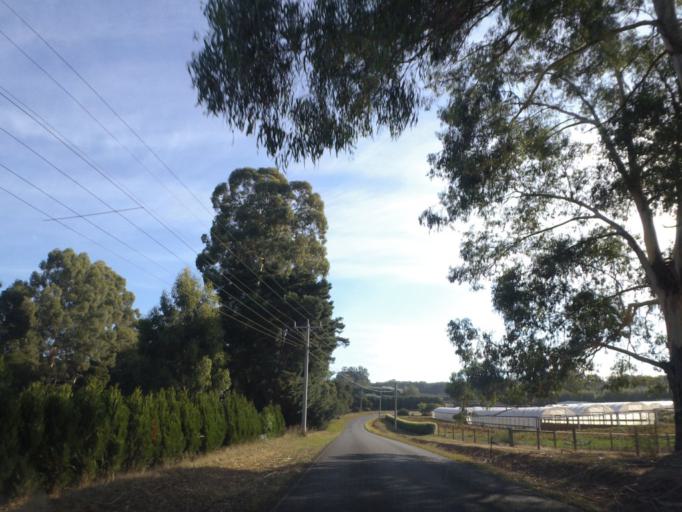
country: AU
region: Victoria
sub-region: Yarra Ranges
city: Monbulk
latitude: -37.8416
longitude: 145.4313
